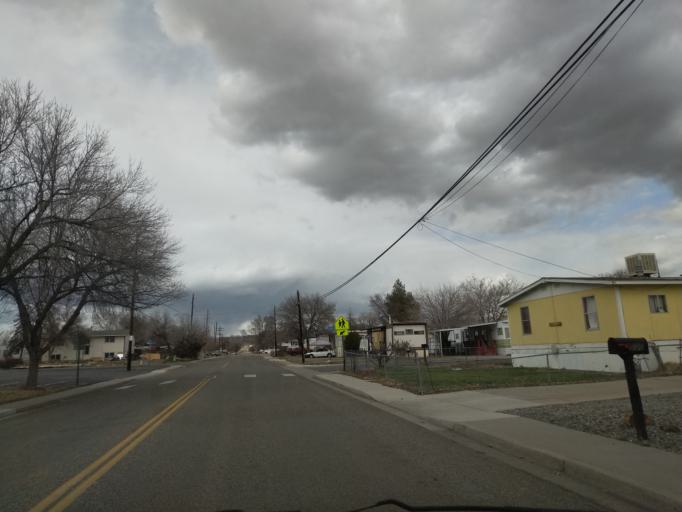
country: US
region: Colorado
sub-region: Mesa County
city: Fruitvale
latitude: 39.0820
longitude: -108.5244
